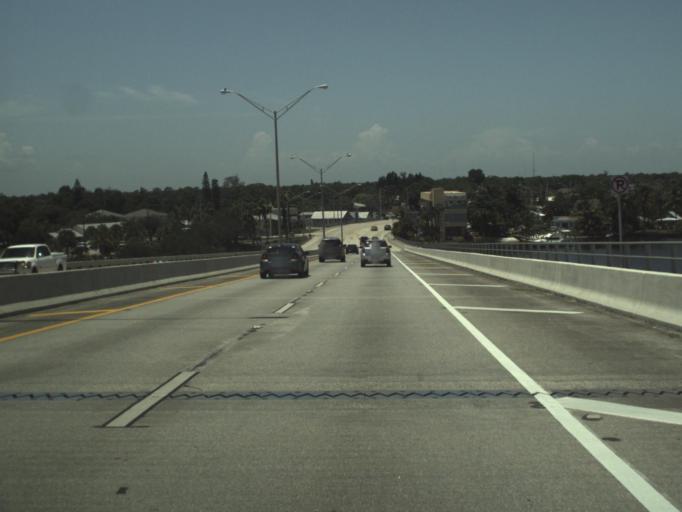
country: US
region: Florida
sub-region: Martin County
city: Palm City
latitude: 27.1738
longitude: -80.2619
